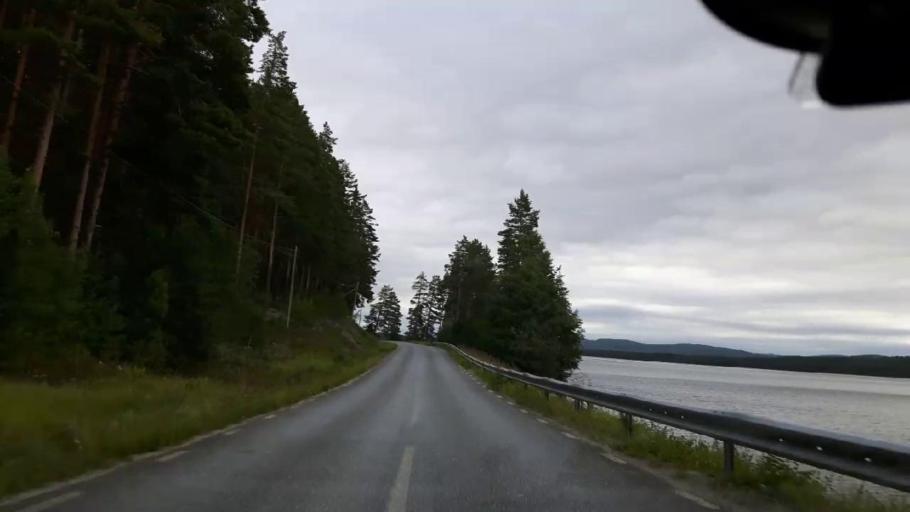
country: SE
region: Jaemtland
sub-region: Braecke Kommun
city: Braecke
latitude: 62.8643
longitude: 15.6195
